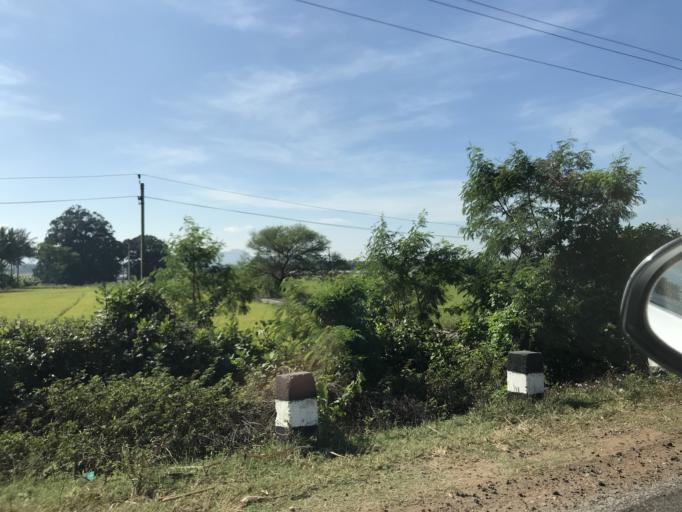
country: IN
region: Karnataka
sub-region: Mysore
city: Heggadadevankote
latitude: 12.1200
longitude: 76.4229
